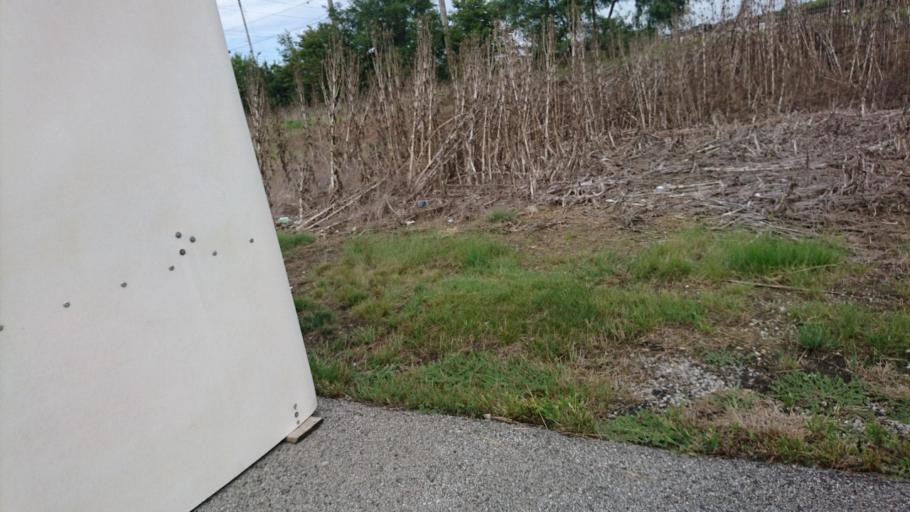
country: US
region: Illinois
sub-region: Sangamon County
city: Southern View
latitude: 39.7416
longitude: -89.6681
